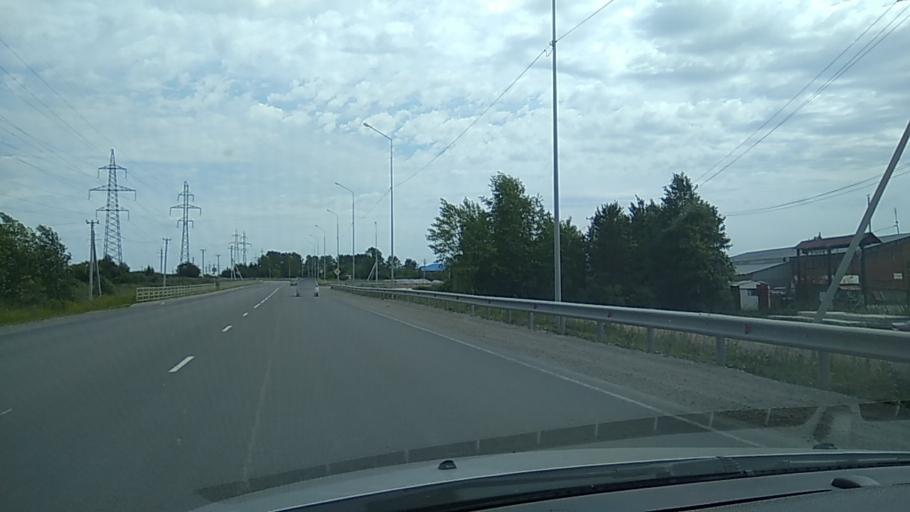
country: RU
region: Sverdlovsk
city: Verkhnyaya Pyshma
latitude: 56.9477
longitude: 60.5991
